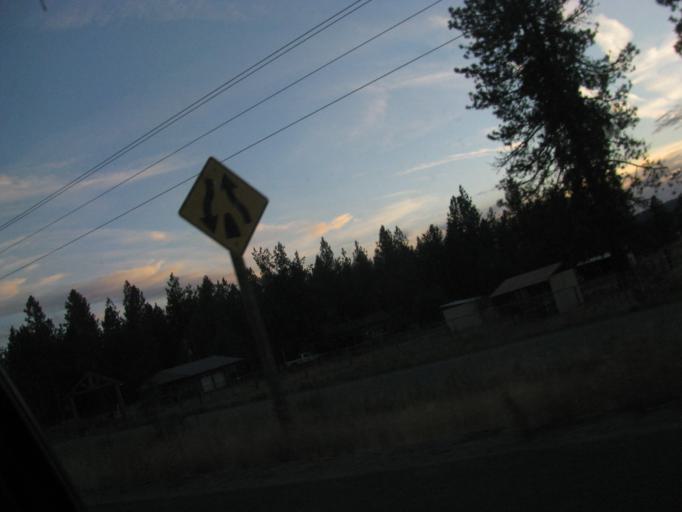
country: US
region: Washington
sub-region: Spokane County
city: Mead
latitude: 47.8091
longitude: -117.3473
